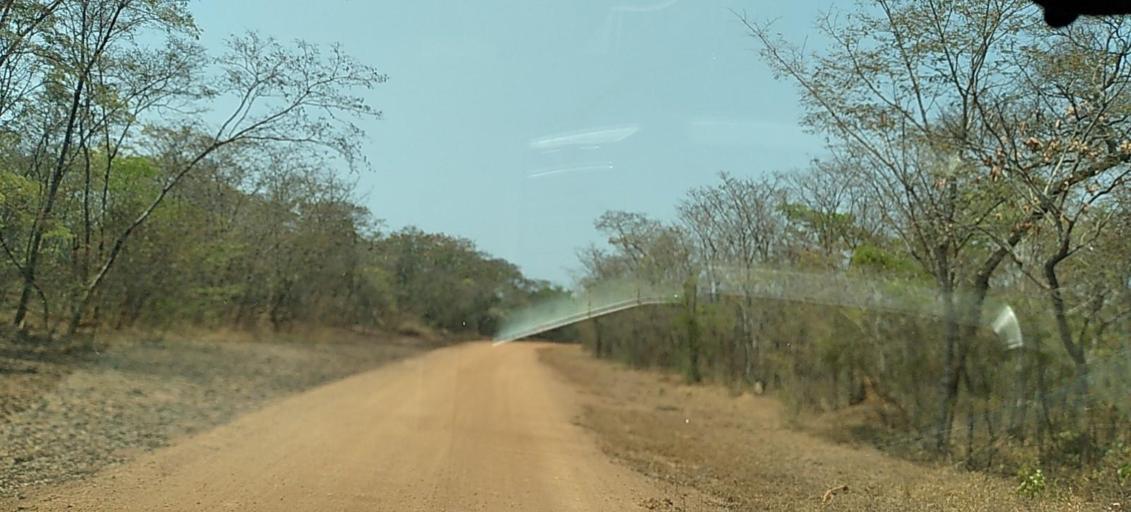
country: ZM
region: Central
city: Mumbwa
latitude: -14.2654
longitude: 26.5179
